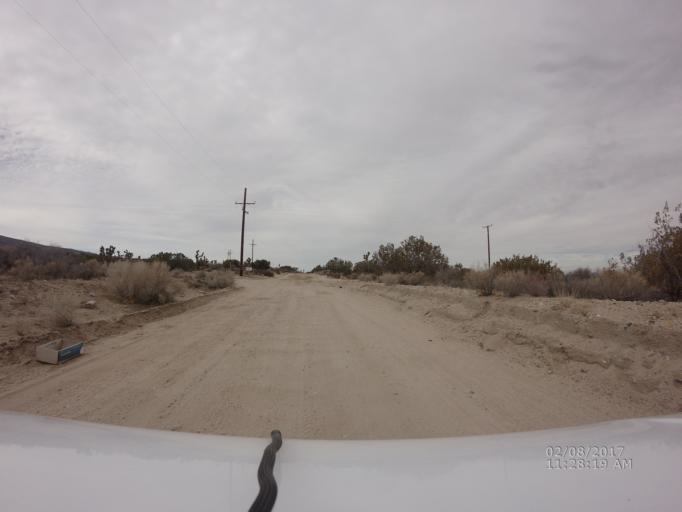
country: US
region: California
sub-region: San Bernardino County
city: Pinon Hills
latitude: 34.4598
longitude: -117.6858
